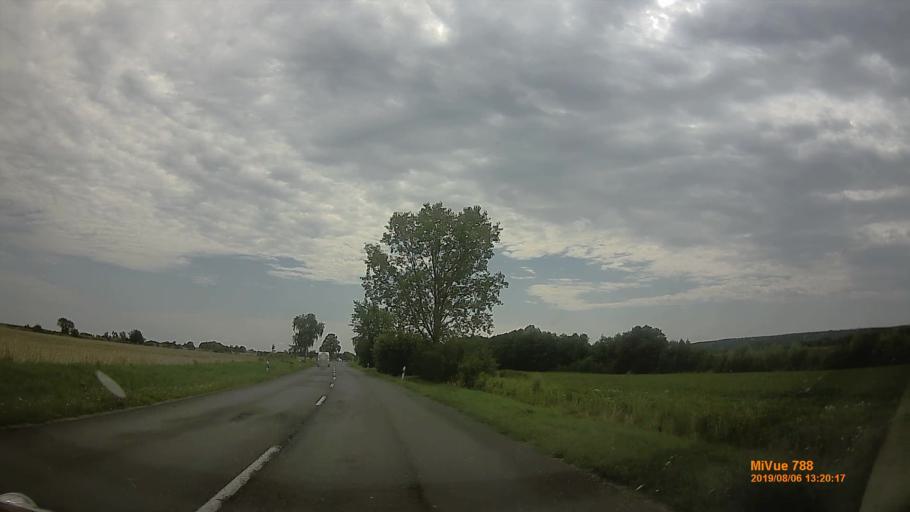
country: HU
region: Vas
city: Koszeg
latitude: 47.3553
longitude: 16.5678
